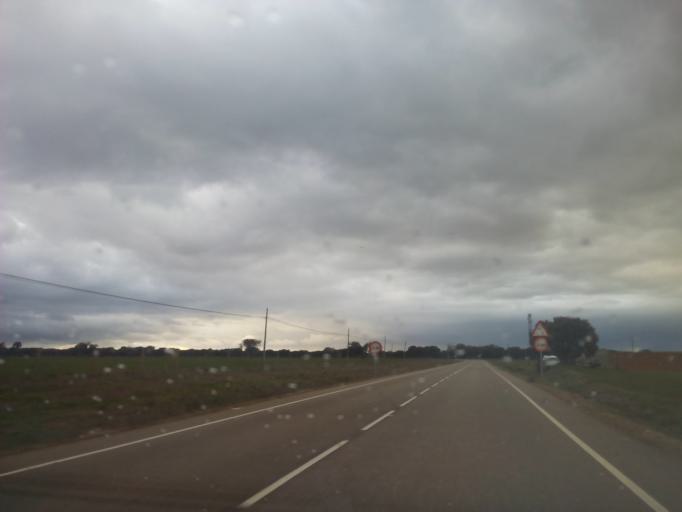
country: ES
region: Castille and Leon
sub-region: Provincia de Salamanca
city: Abusejo
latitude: 40.7204
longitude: -6.1496
